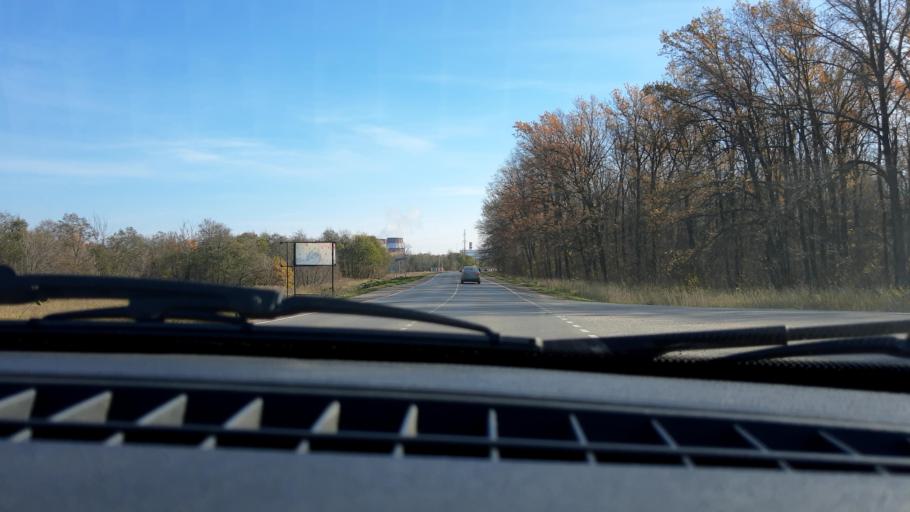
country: RU
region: Bashkortostan
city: Mikhaylovka
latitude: 54.8089
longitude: 55.8151
